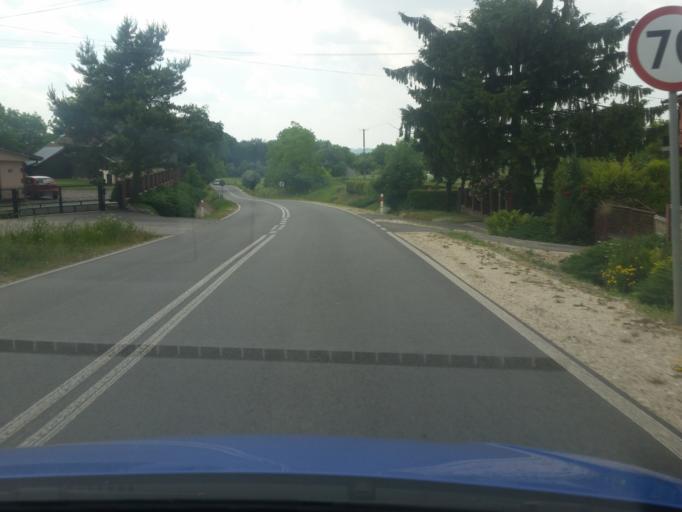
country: PL
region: Swietokrzyskie
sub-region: Powiat kazimierski
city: Czarnocin
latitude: 50.3093
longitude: 20.5253
